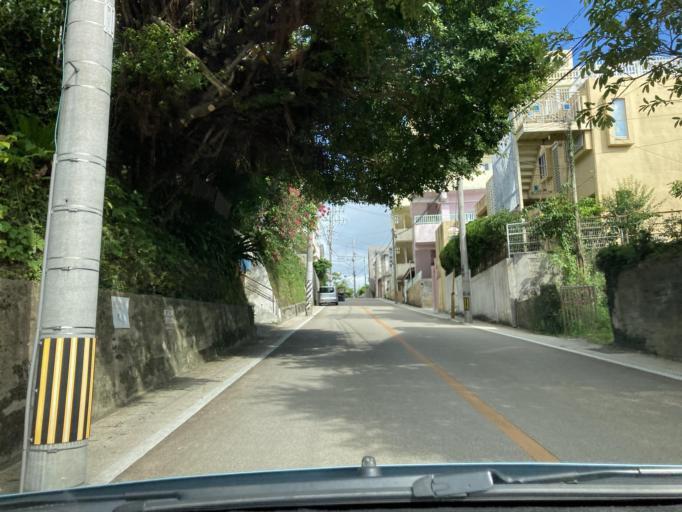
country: JP
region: Okinawa
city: Naha-shi
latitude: 26.2158
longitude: 127.7180
